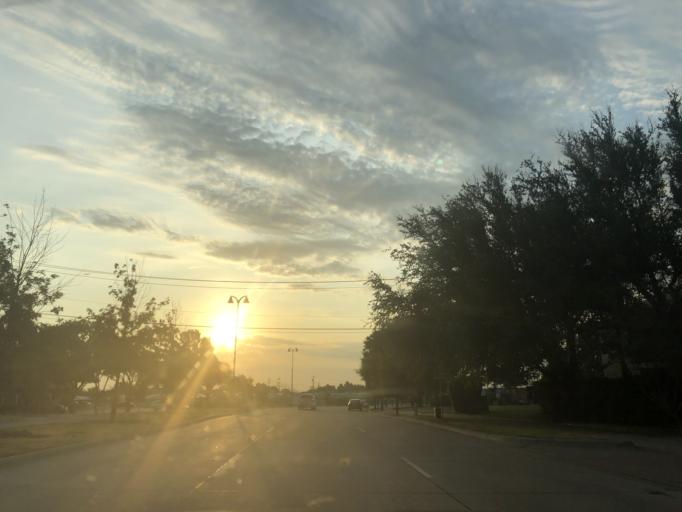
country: US
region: Texas
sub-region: Tarrant County
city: Arlington
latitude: 32.7645
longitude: -97.0889
